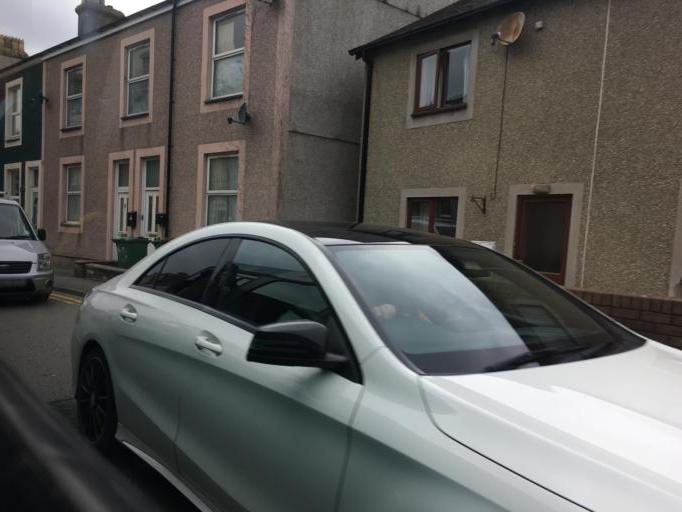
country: GB
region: Wales
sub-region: Gwynedd
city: Y Felinheli
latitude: 53.1852
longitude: -4.2084
